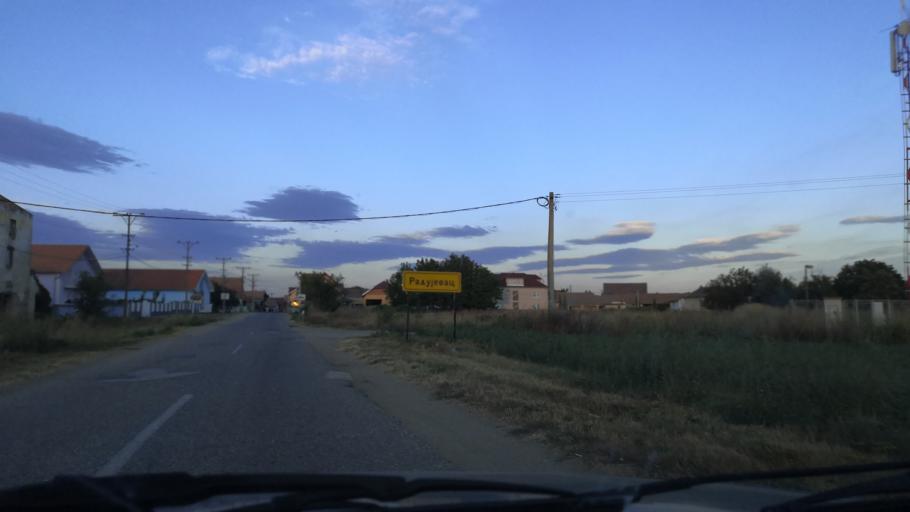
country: RO
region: Mehedinti
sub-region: Comuna Gruia
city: Gruia
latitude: 44.2675
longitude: 22.6660
